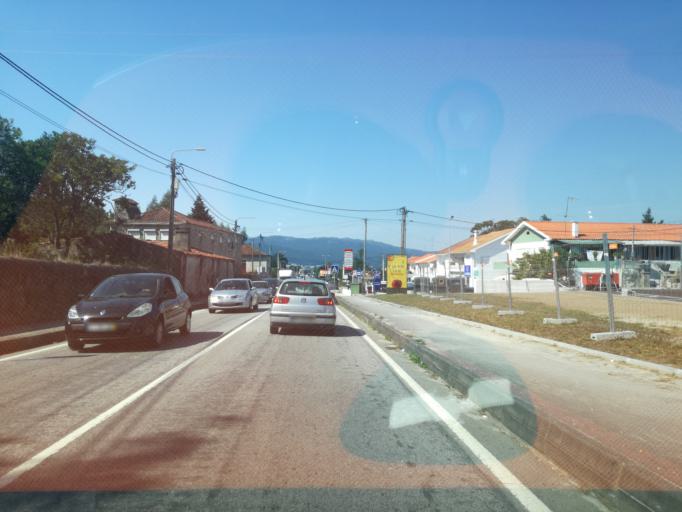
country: PT
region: Viana do Castelo
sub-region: Viana do Castelo
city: Darque
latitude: 41.6786
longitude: -8.7843
